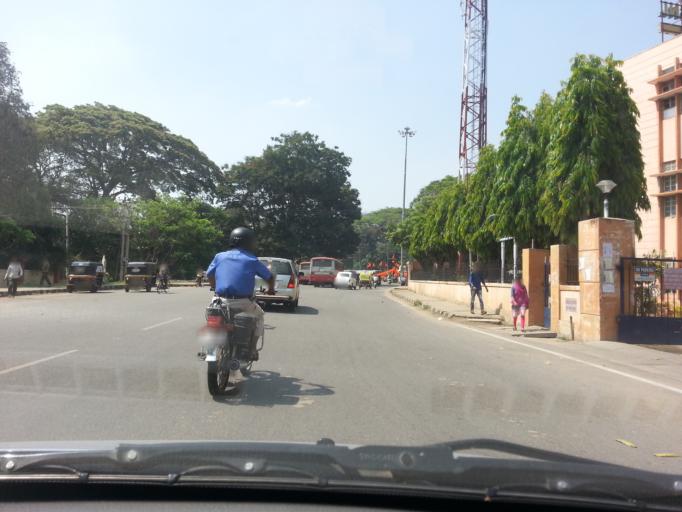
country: IN
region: Karnataka
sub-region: Mysore
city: Mysore
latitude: 12.3082
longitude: 76.6608
